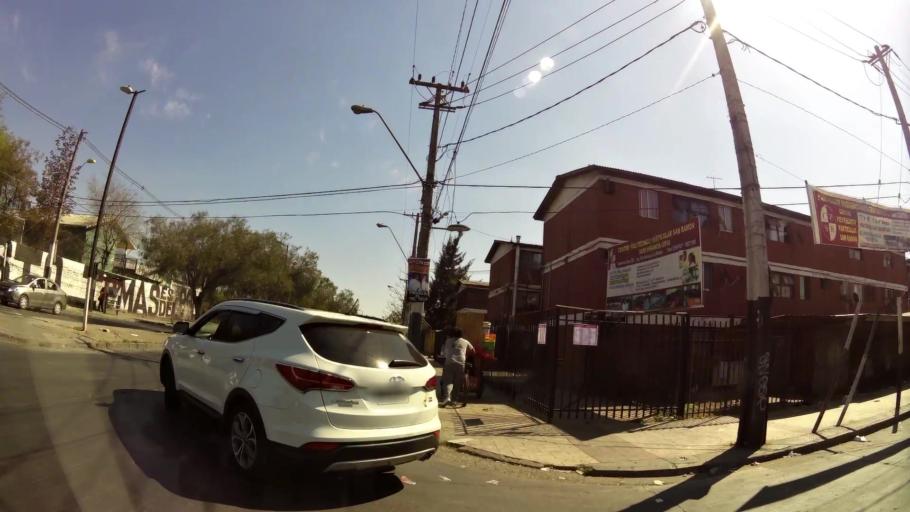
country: CL
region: Santiago Metropolitan
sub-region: Provincia de Santiago
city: La Pintana
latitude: -33.5582
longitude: -70.6236
